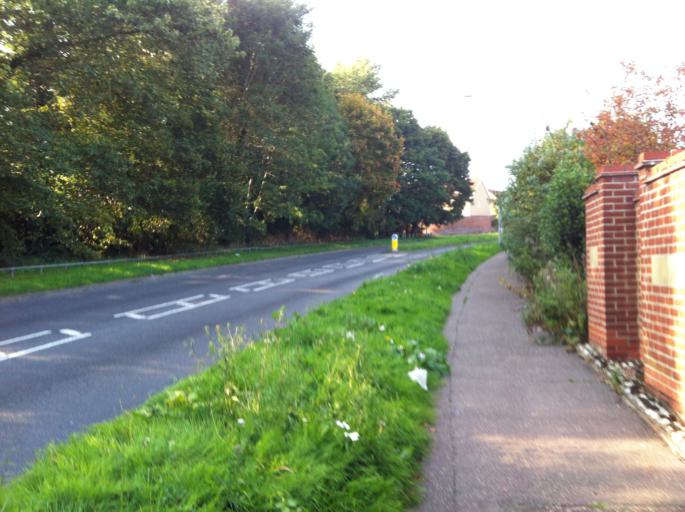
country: GB
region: England
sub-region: Norfolk
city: Bowthorpe
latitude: 52.6382
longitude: 1.2094
